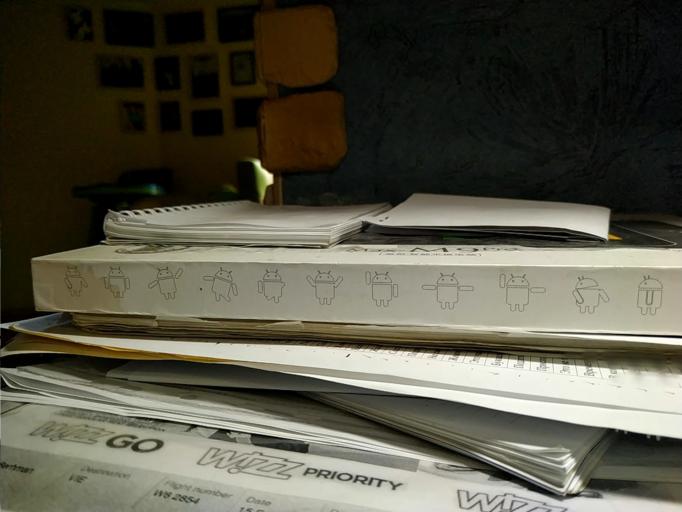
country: RU
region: Novgorod
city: Poddor'ye
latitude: 57.5233
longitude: 30.9135
